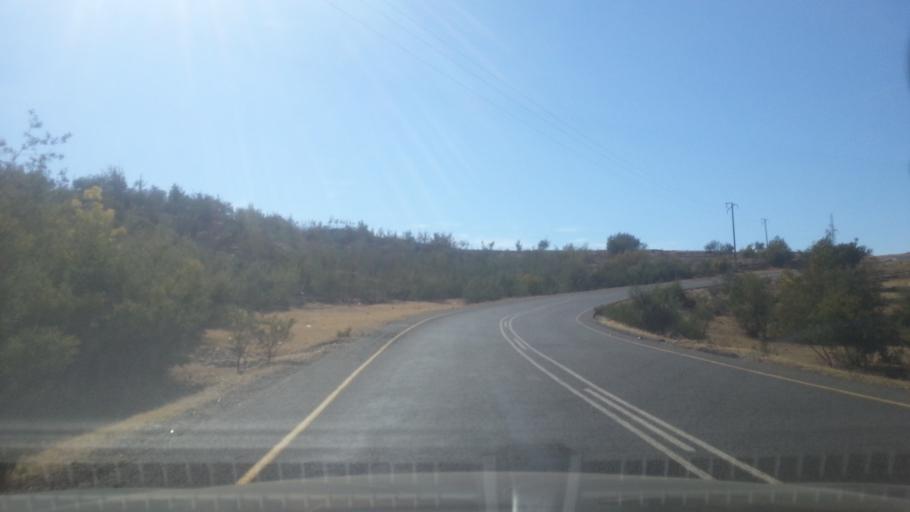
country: LS
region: Maseru
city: Maseru
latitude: -29.5011
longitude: 27.5685
